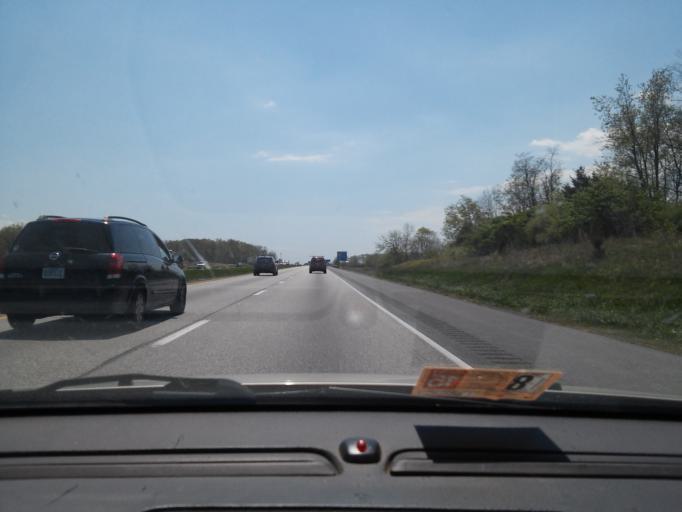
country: US
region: Pennsylvania
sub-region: Franklin County
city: Greencastle
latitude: 39.7711
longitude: -77.7199
